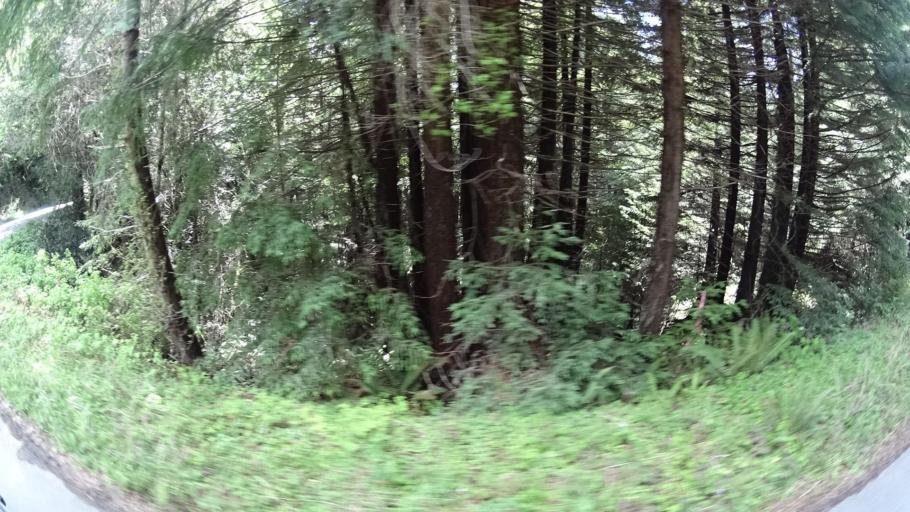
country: US
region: California
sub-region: Humboldt County
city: Blue Lake
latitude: 40.8267
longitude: -123.8943
